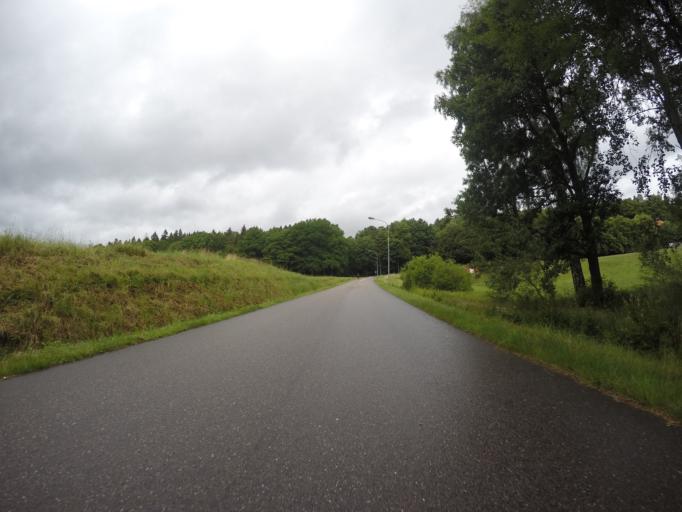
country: SE
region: Vaestra Goetaland
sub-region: Trollhattan
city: Sjuntorp
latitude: 58.2006
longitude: 12.2305
